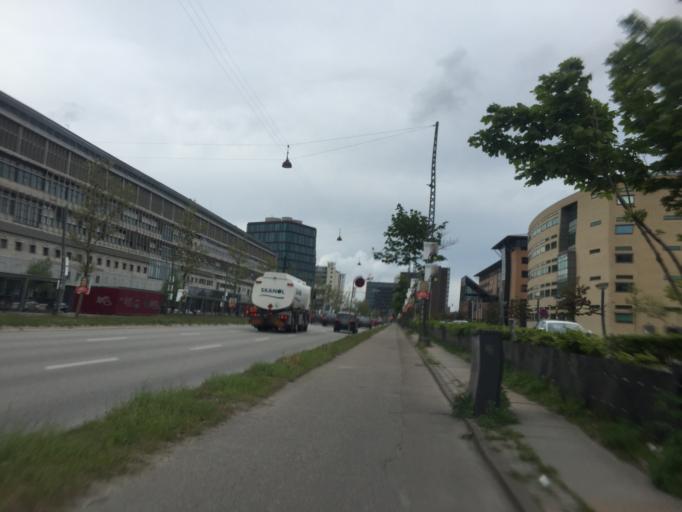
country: DK
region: Capital Region
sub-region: Kobenhavn
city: Copenhagen
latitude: 55.6660
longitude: 12.5679
